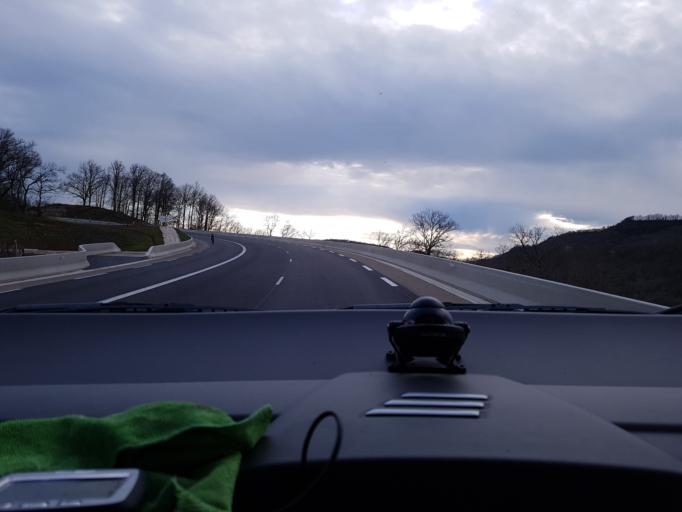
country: FR
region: Midi-Pyrenees
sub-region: Departement de l'Aveyron
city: Espalion
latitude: 44.5266
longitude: 2.7358
